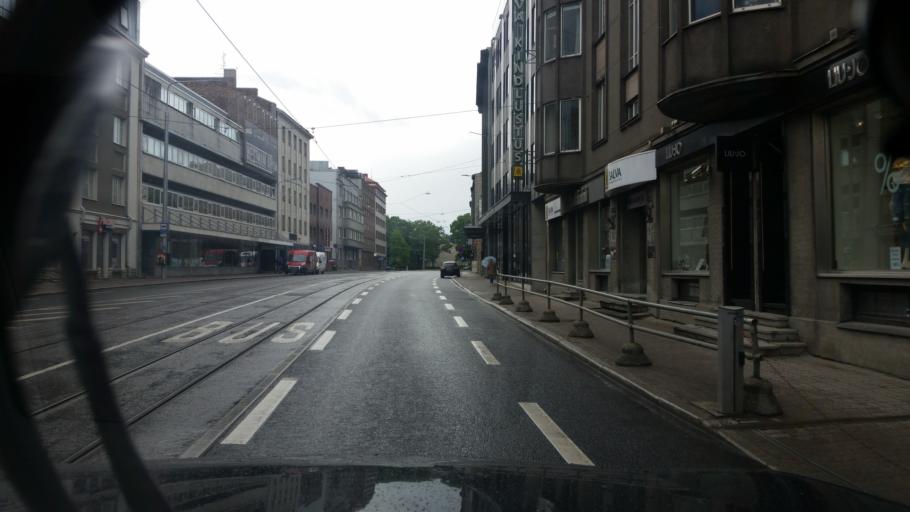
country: EE
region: Harju
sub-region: Tallinna linn
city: Tallinn
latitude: 59.4324
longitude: 24.7456
